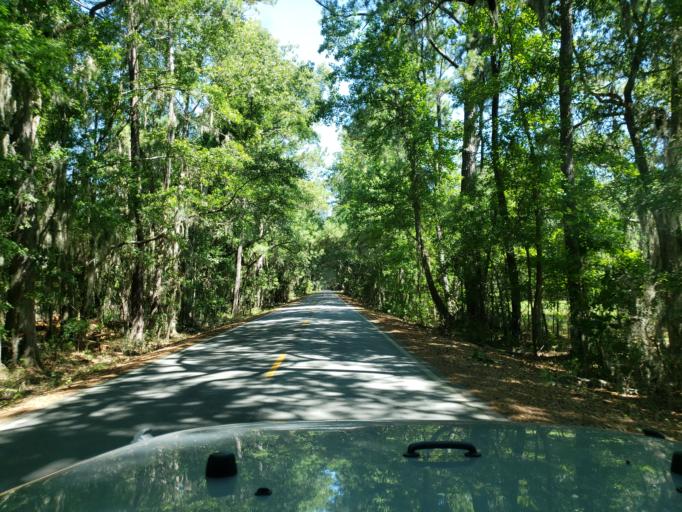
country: US
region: Georgia
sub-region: Chatham County
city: Georgetown
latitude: 31.9565
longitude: -81.2166
